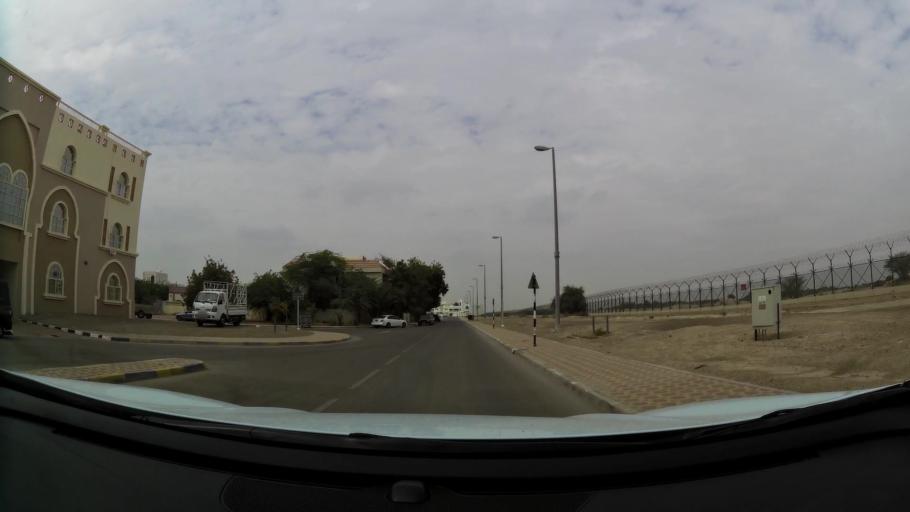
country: OM
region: Al Buraimi
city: Al Buraymi
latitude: 24.2261
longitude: 55.7886
